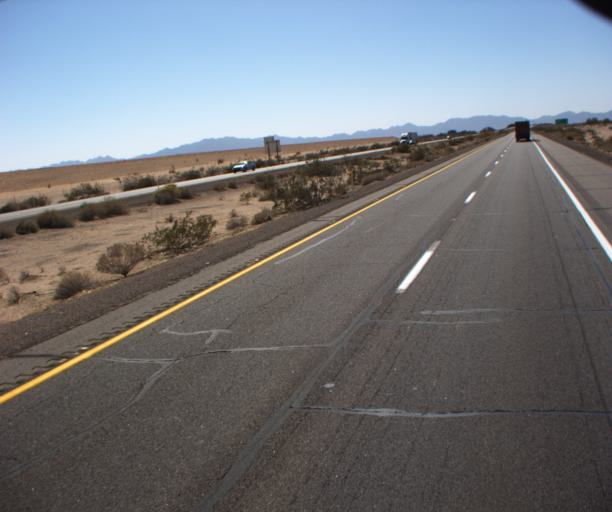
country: US
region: Arizona
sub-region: Yuma County
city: Wellton
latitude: 32.6792
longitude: -114.0343
